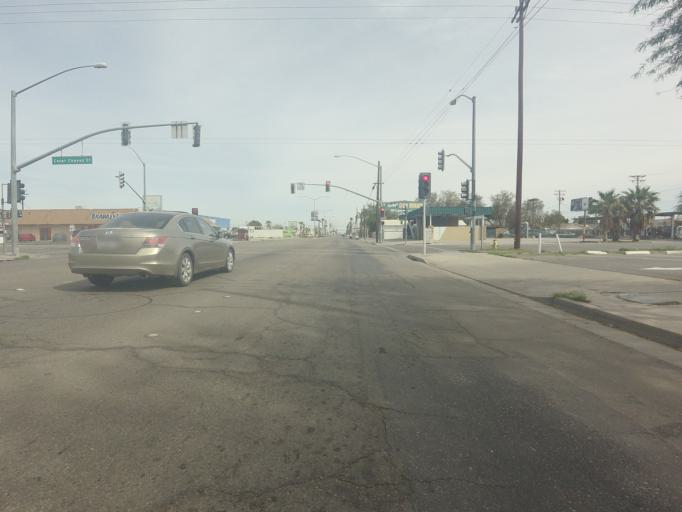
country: US
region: California
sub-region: Imperial County
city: Brawley
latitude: 32.9786
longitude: -115.5267
